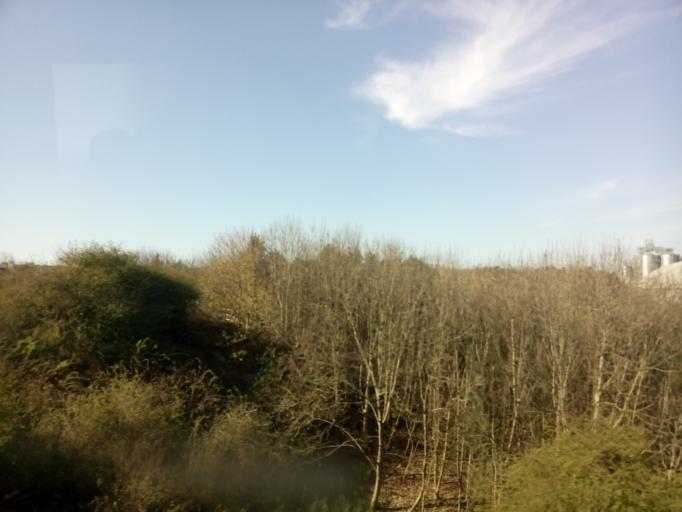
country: GB
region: England
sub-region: Northumberland
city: Berwick-Upon-Tweed
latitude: 55.7617
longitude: -2.0122
